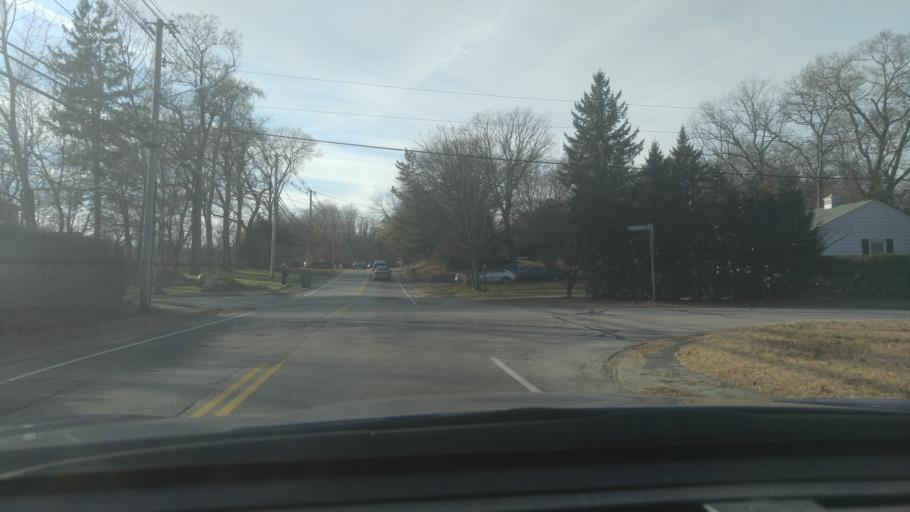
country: US
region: Rhode Island
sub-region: Kent County
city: East Greenwich
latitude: 41.6851
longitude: -71.4663
